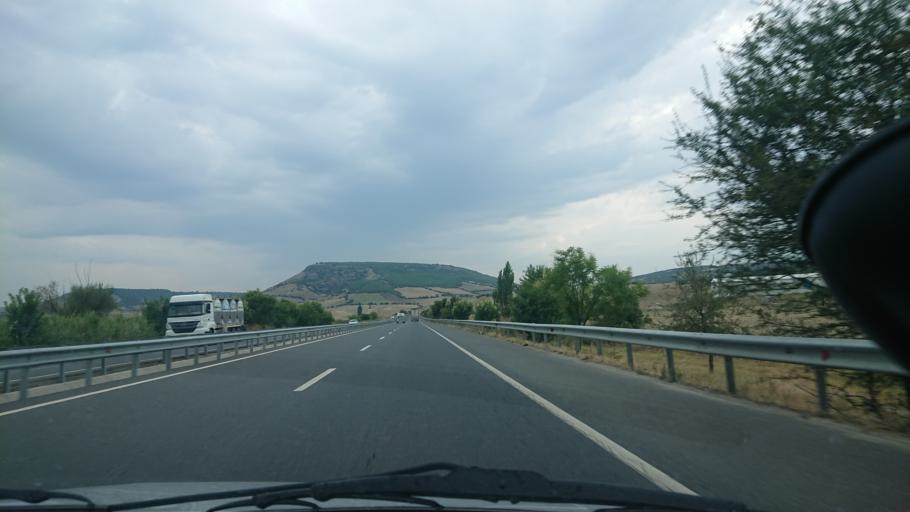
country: TR
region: Manisa
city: Selendi
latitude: 38.6169
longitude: 28.8831
